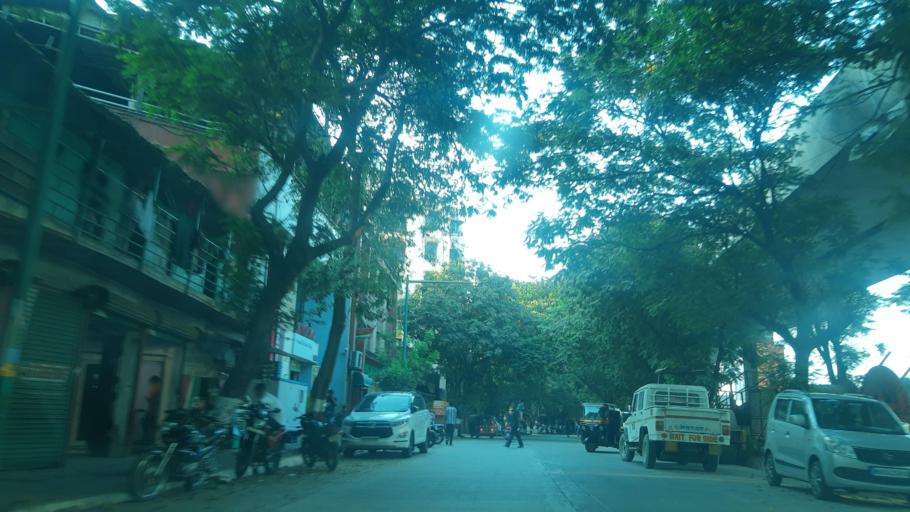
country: IN
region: Maharashtra
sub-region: Thane
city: Thane
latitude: 19.1966
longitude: 72.9621
